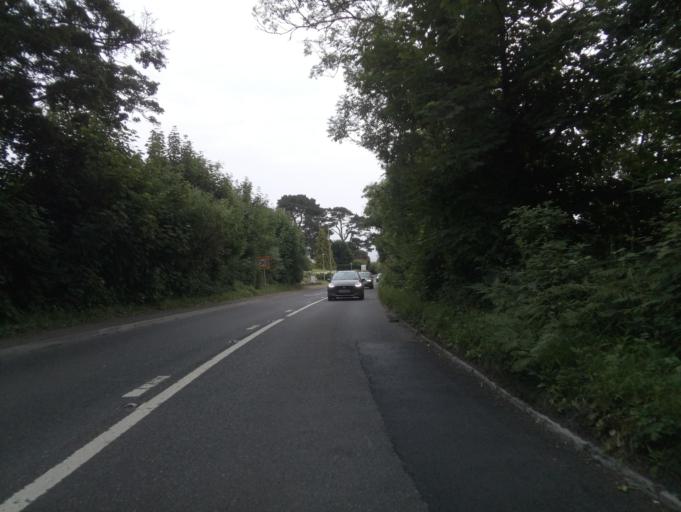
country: GB
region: England
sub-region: Dorset
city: Lyme Regis
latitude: 50.7360
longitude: -2.9319
